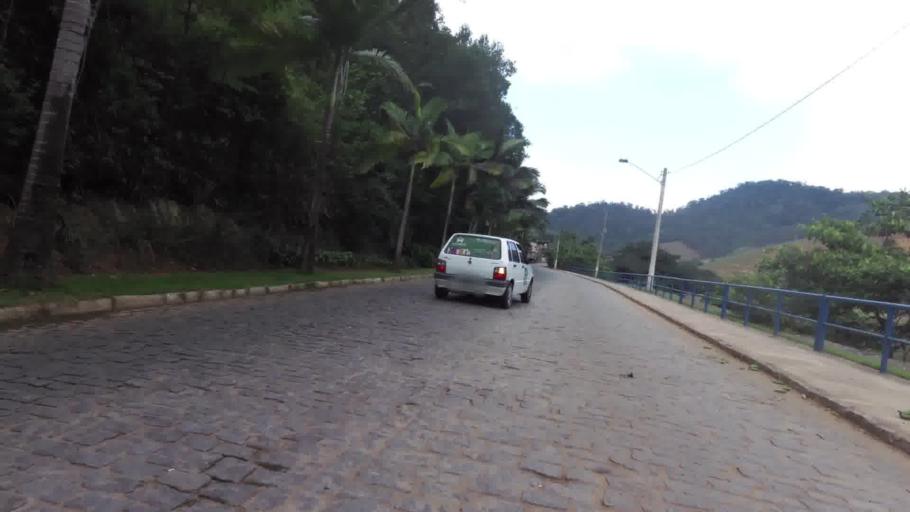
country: BR
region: Espirito Santo
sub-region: Alfredo Chaves
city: Alfredo Chaves
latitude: -20.6267
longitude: -40.7679
